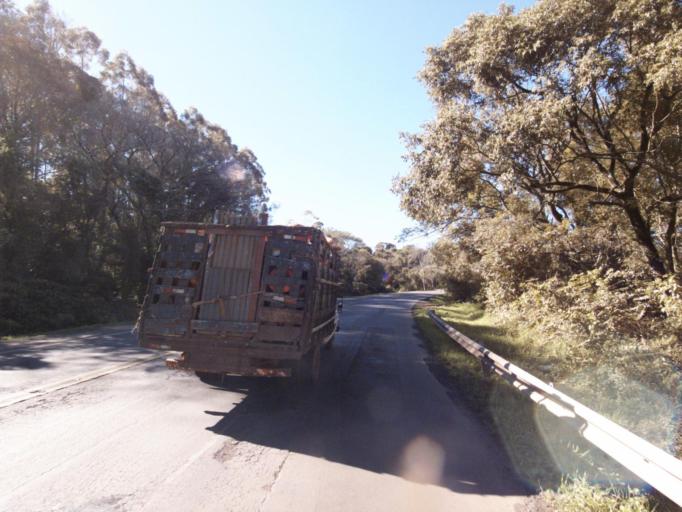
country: BR
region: Santa Catarina
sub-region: Chapeco
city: Chapeco
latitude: -26.9312
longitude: -52.8279
